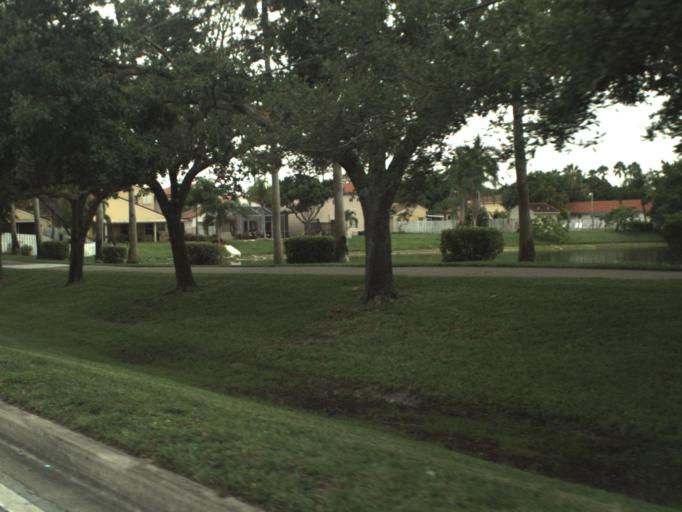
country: US
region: Florida
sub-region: Broward County
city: Pine Island Ridge
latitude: 26.1414
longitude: -80.3144
